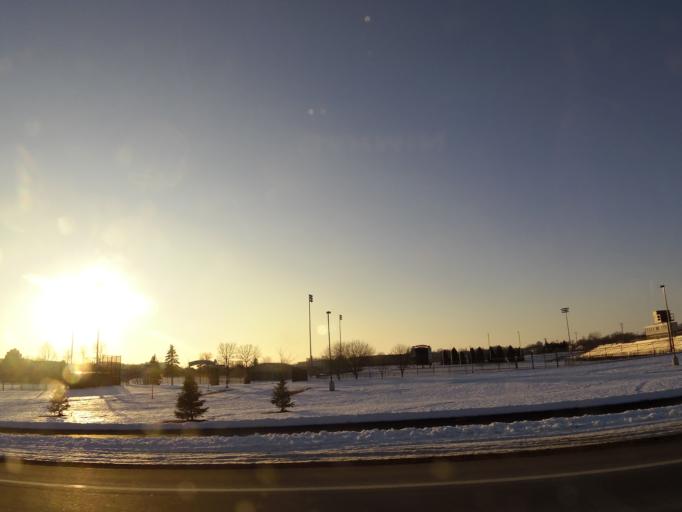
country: US
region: Minnesota
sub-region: Scott County
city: Shakopee
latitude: 44.7845
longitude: -93.5202
